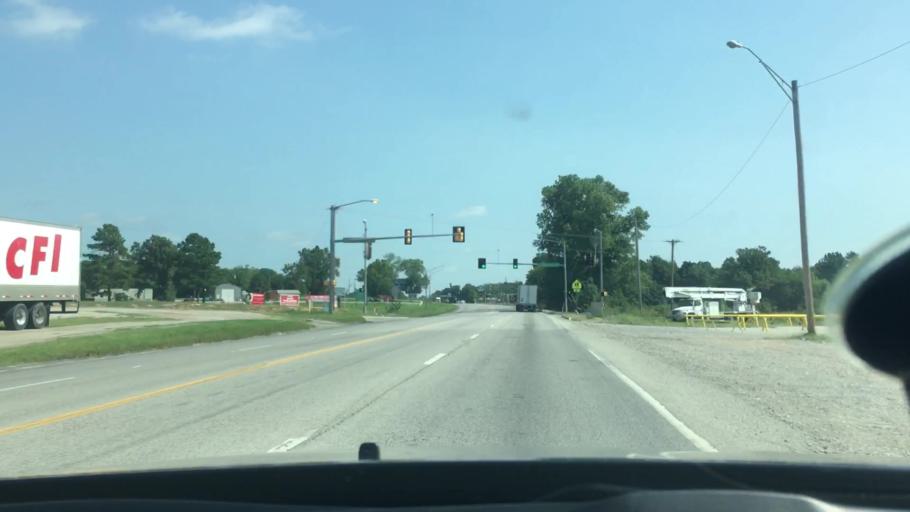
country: US
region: Oklahoma
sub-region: Atoka County
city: Atoka
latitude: 34.3161
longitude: -96.1697
